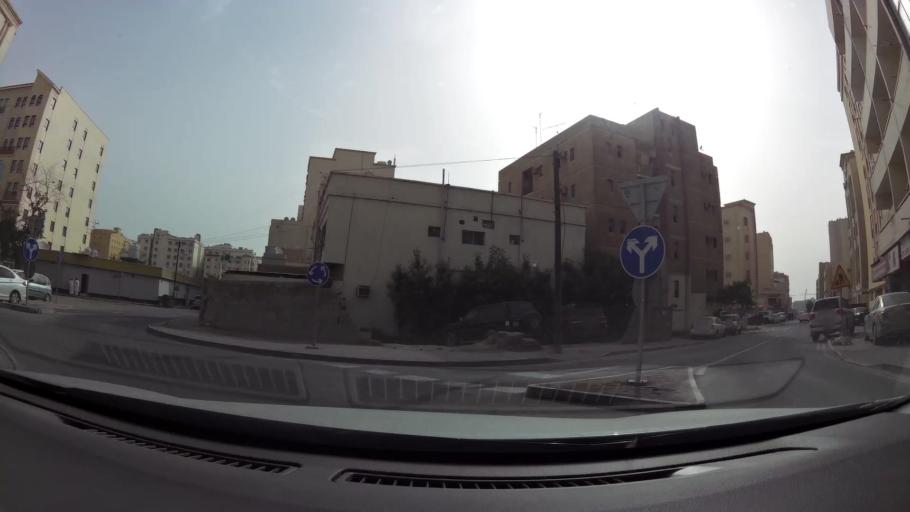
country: QA
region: Baladiyat ad Dawhah
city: Doha
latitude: 25.2773
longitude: 51.5443
